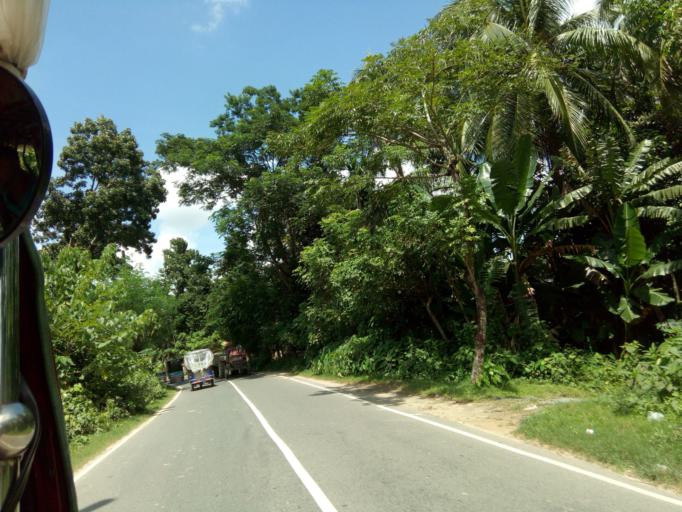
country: BD
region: Dhaka
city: Tungipara
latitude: 22.9941
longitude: 89.8149
